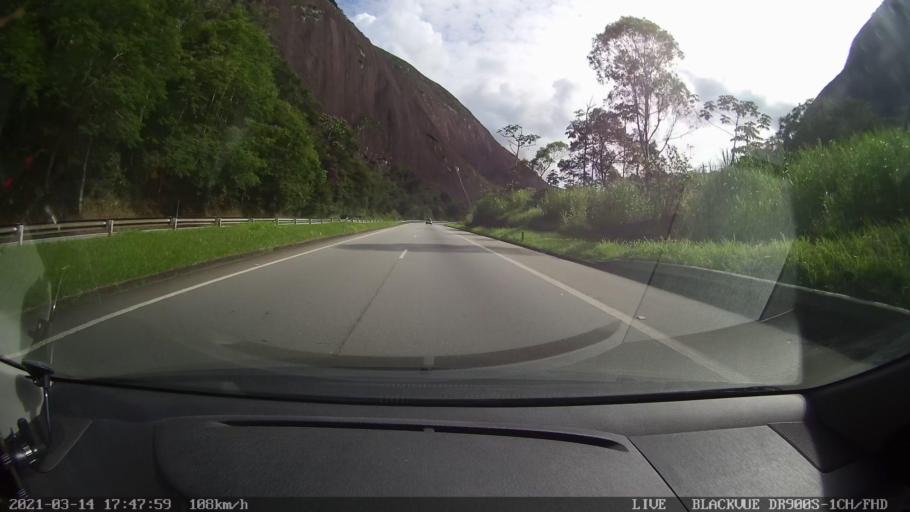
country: BR
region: Rio de Janeiro
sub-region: Petropolis
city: Petropolis
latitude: -22.4396
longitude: -43.1863
